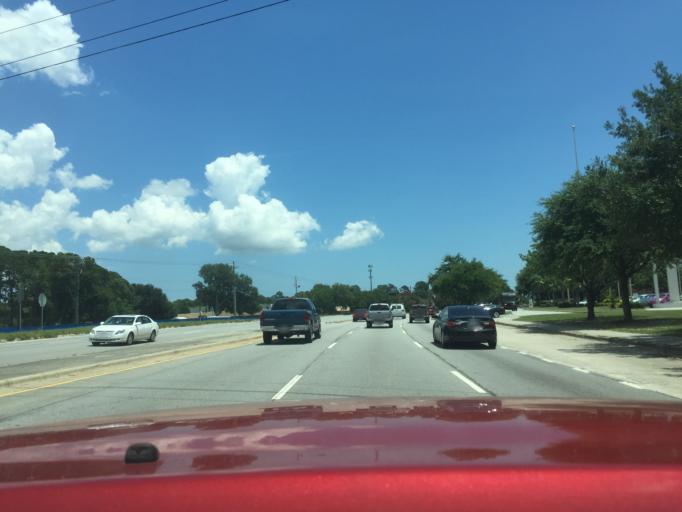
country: US
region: Georgia
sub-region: Chatham County
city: Montgomery
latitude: 31.9835
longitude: -81.1566
